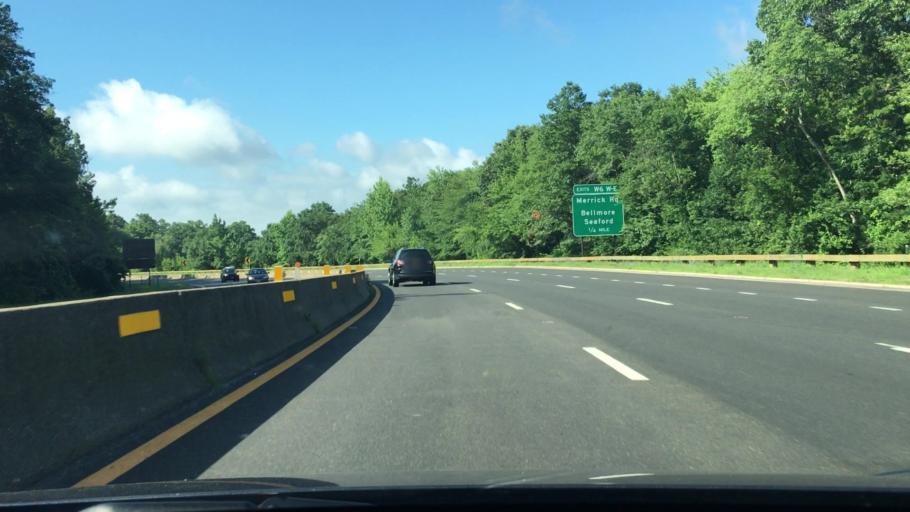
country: US
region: New York
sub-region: Nassau County
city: Bellmore
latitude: 40.6691
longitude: -73.5156
